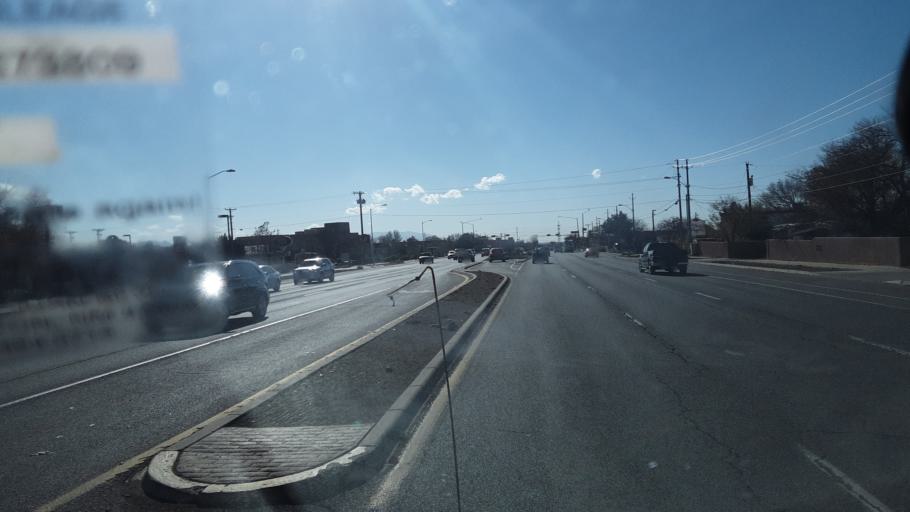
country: US
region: New Mexico
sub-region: Santa Fe County
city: Agua Fria
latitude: 35.6455
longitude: -106.0073
